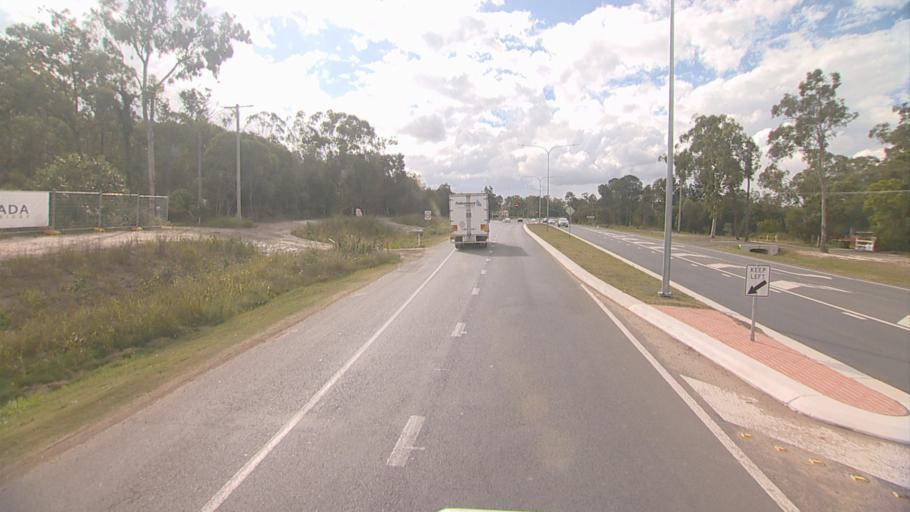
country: AU
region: Queensland
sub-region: Logan
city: Logan Reserve
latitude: -27.7109
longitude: 153.0934
